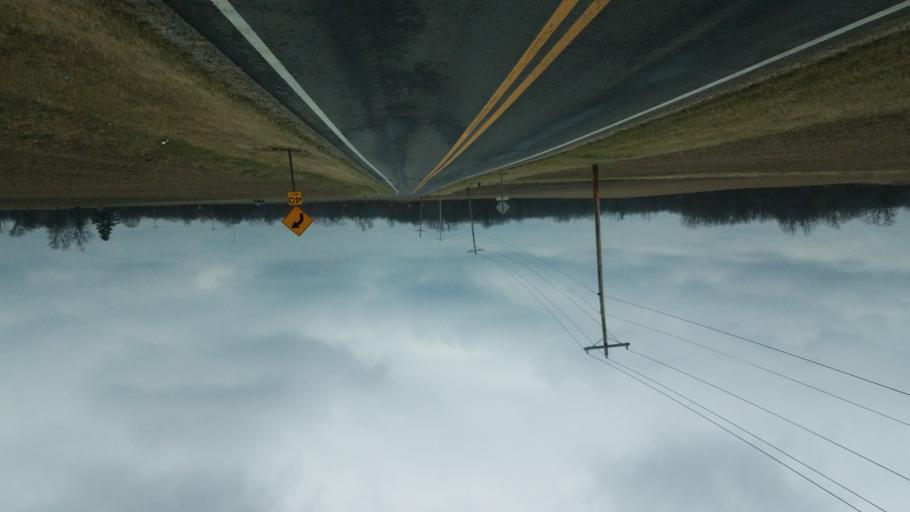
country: US
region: Ohio
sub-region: Delaware County
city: Ashley
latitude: 40.3838
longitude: -82.9444
